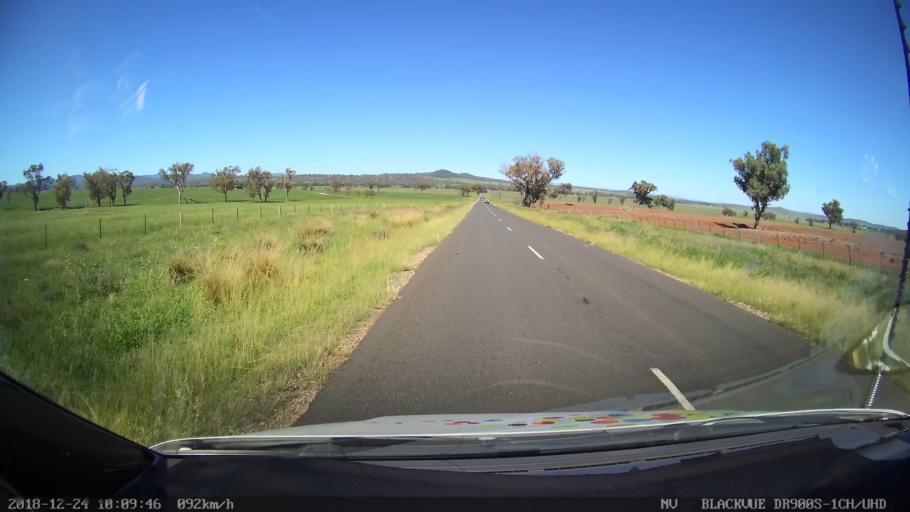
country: AU
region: New South Wales
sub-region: Liverpool Plains
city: Quirindi
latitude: -31.6650
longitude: 150.6858
